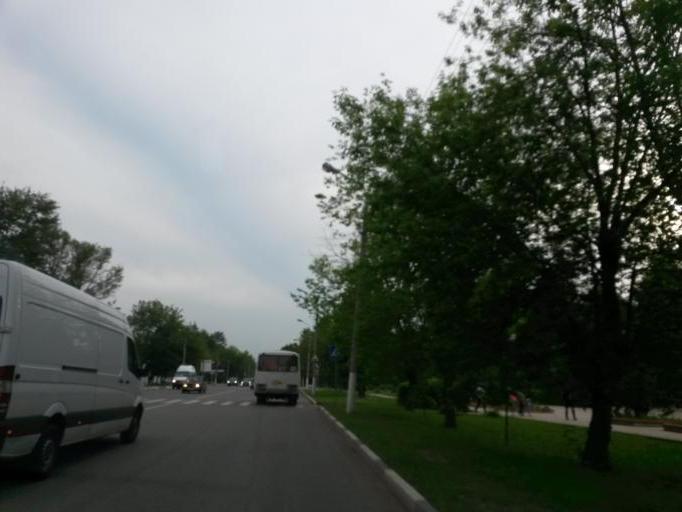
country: RU
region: Moskovskaya
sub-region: Chekhovskiy Rayon
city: Chekhov
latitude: 55.1441
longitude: 37.4699
